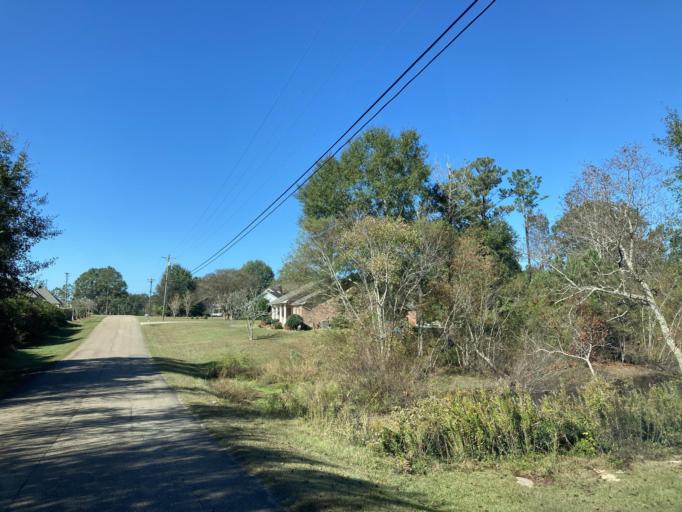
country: US
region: Mississippi
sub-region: Lamar County
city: West Hattiesburg
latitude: 31.2994
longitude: -89.4146
